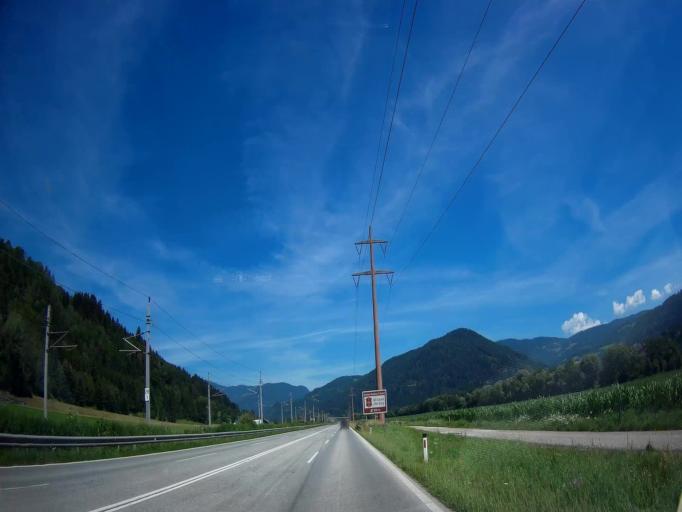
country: AT
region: Carinthia
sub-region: Politischer Bezirk Sankt Veit an der Glan
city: Micheldorf
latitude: 46.9306
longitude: 14.4273
